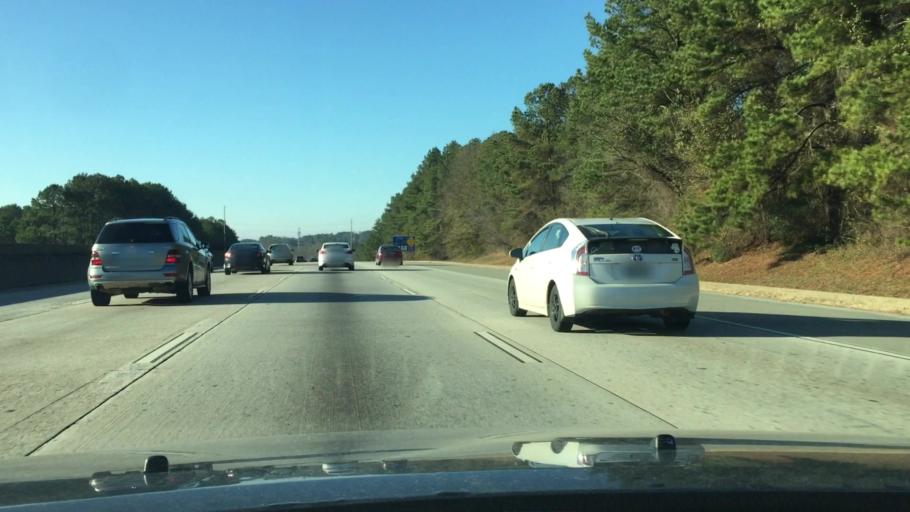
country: US
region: Georgia
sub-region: Fulton County
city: Alpharetta
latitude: 34.0422
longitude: -84.3092
